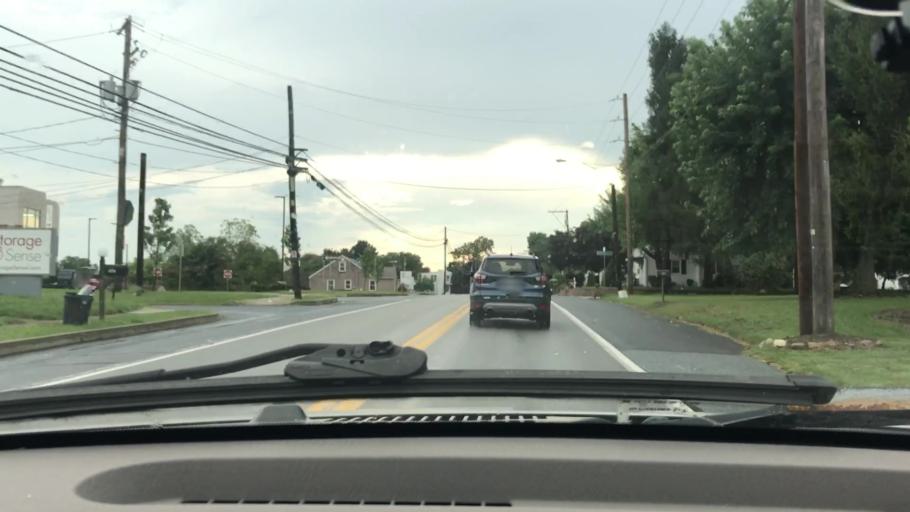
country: US
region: Pennsylvania
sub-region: Dauphin County
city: Colonial Park
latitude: 40.2929
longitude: -76.7966
